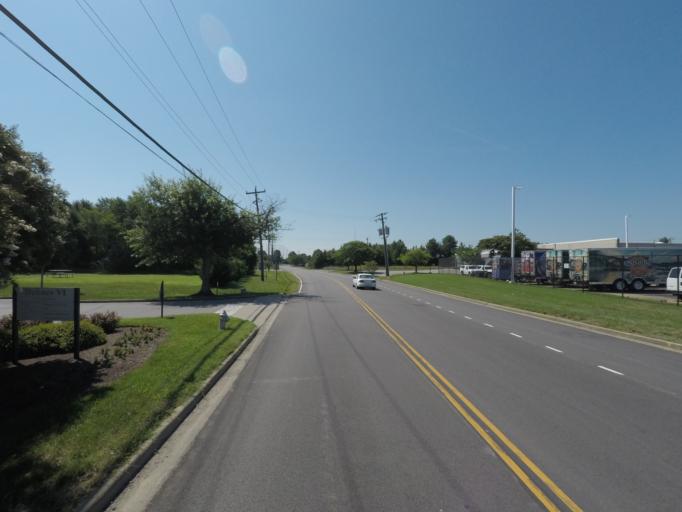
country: US
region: Virginia
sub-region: Henrico County
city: Dumbarton
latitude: 37.5859
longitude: -77.4835
